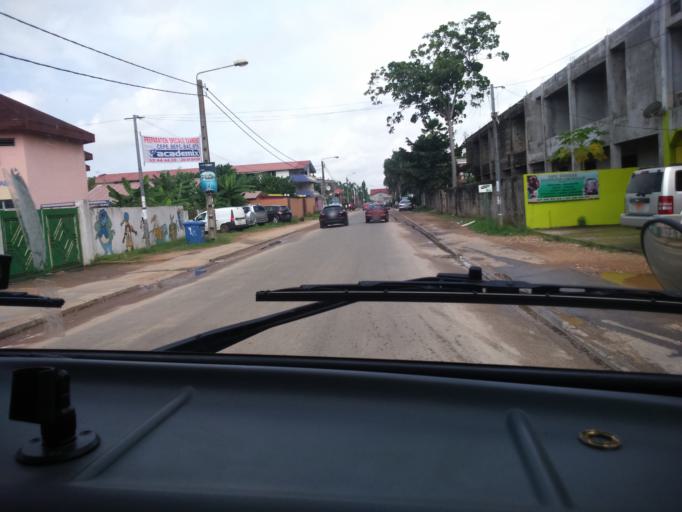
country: CI
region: Lagunes
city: Abidjan
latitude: 5.3570
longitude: -3.9784
